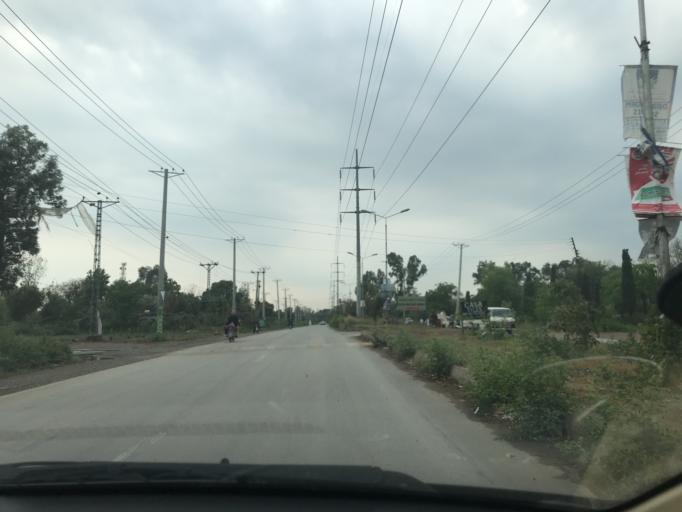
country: PK
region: Punjab
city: Rawalpindi
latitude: 33.6773
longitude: 73.1492
